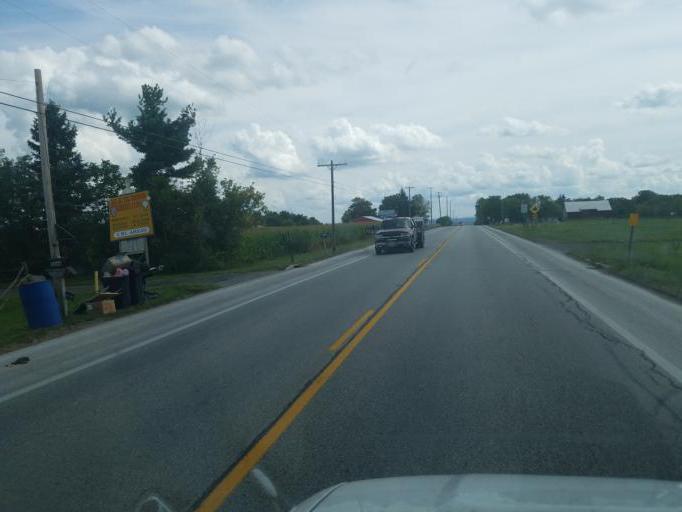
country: US
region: Ohio
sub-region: Geauga County
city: Middlefield
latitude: 41.4588
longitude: -80.9987
